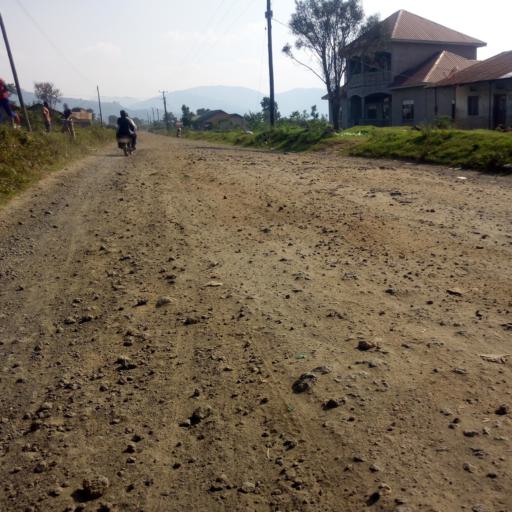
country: UG
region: Western Region
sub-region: Kisoro District
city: Kisoro
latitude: -1.2419
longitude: 29.7138
